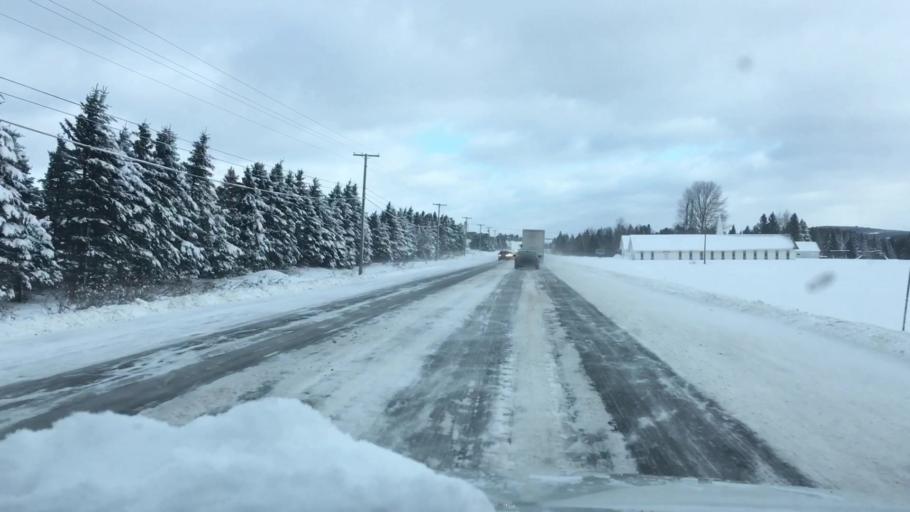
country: US
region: Maine
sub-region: Aroostook County
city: Presque Isle
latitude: 46.7345
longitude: -68.0001
